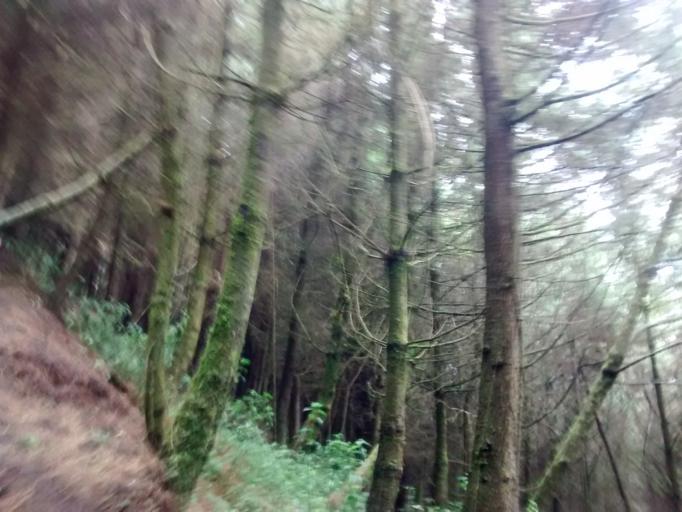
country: GT
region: San Marcos
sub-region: Municipio de San Marcos
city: San Marcos
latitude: 14.9828
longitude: -91.8289
